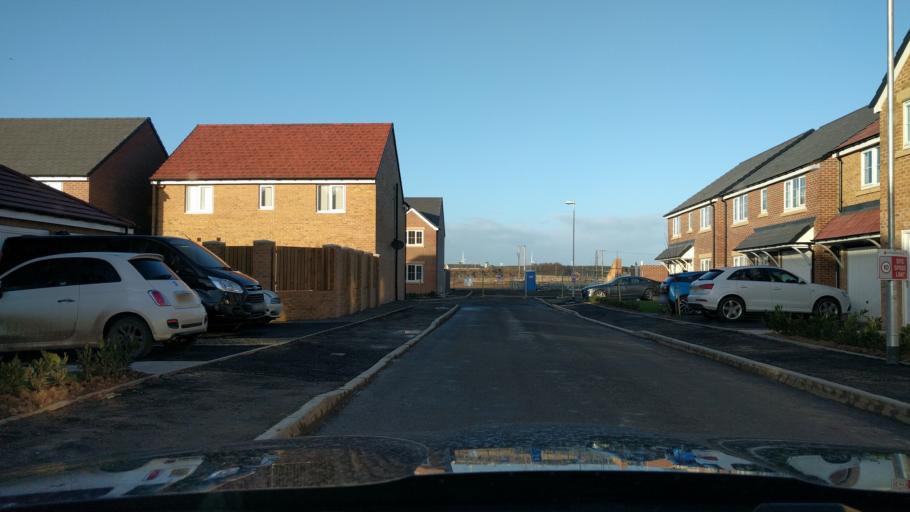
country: GB
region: England
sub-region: Northumberland
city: Newbiggin-by-the-Sea
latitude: 55.1801
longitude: -1.5407
